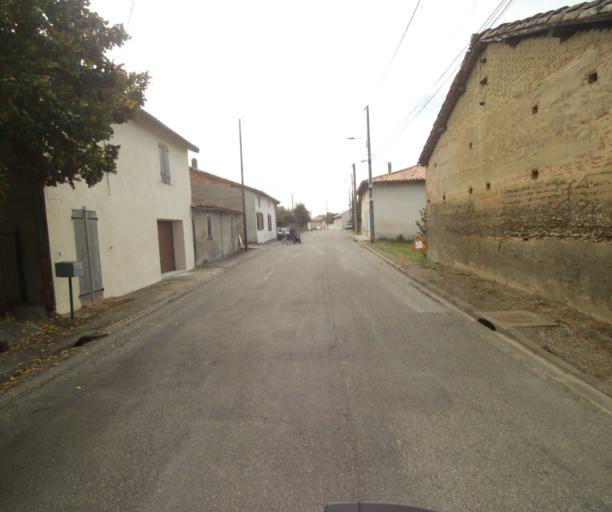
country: FR
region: Midi-Pyrenees
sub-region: Departement du Tarn-et-Garonne
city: Finhan
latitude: 43.9088
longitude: 1.2196
